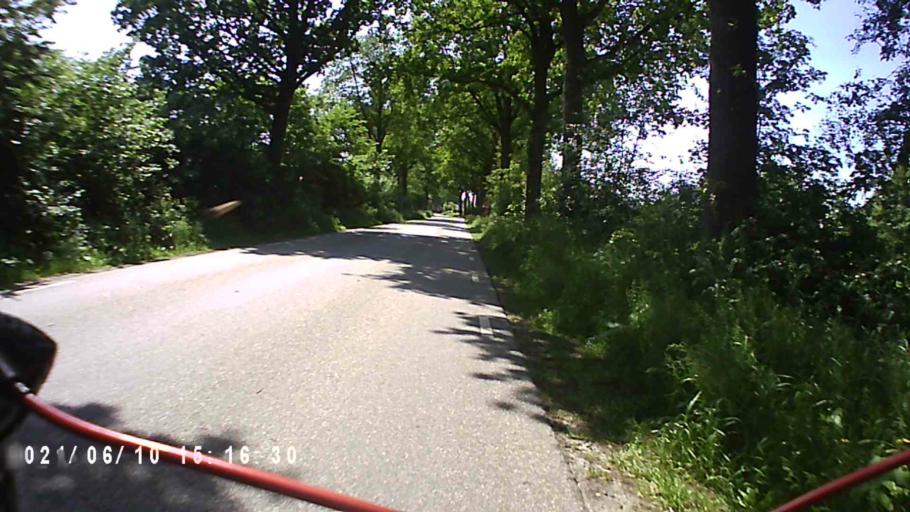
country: NL
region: Friesland
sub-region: Gemeente Achtkarspelen
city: Surhuizum
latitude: 53.1973
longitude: 6.1728
